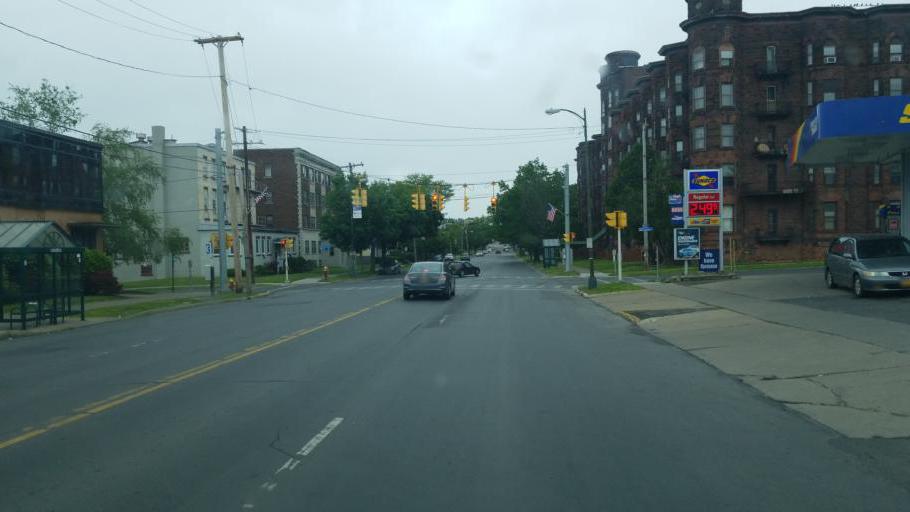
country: US
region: New York
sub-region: Oneida County
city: Utica
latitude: 43.0931
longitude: -75.2481
